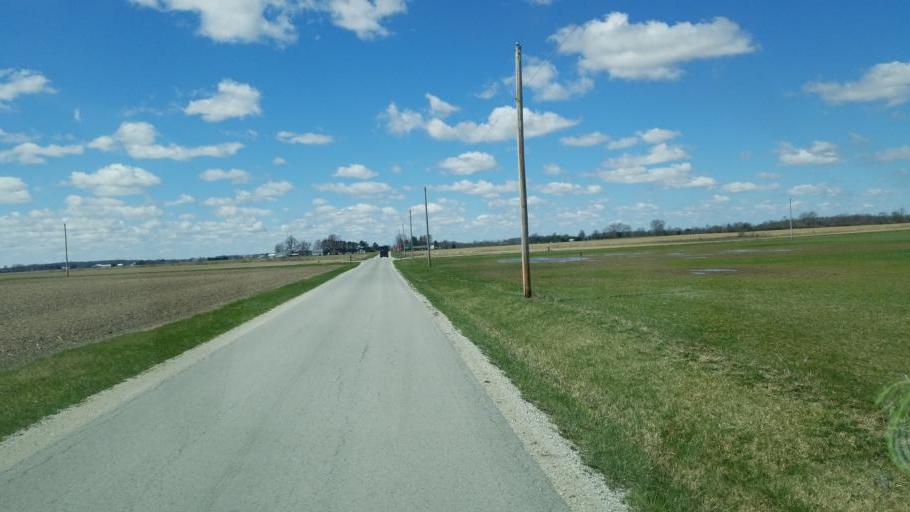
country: US
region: Ohio
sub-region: Seneca County
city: Fostoria
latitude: 41.0941
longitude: -83.5153
